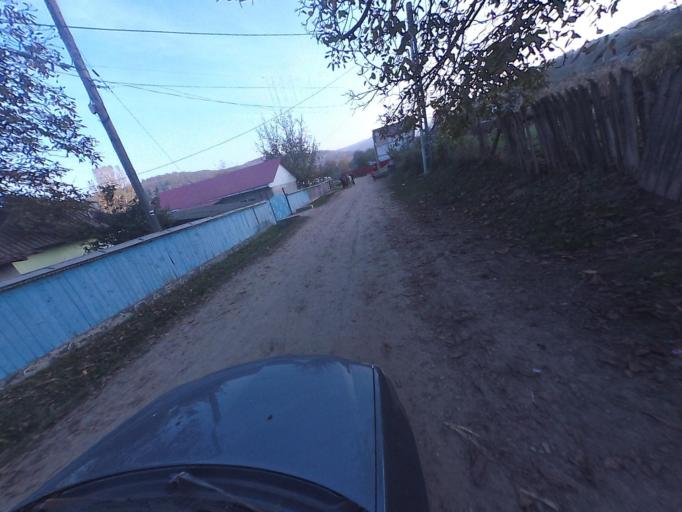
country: RO
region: Vaslui
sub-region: Comuna Bacesti
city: Bacesti
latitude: 46.8008
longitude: 27.2244
